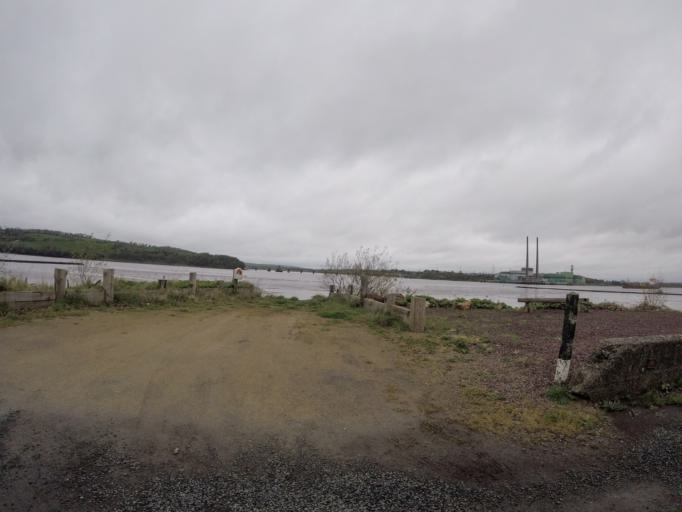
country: IE
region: Munster
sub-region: Waterford
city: Waterford
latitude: 52.2717
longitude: -7.0021
